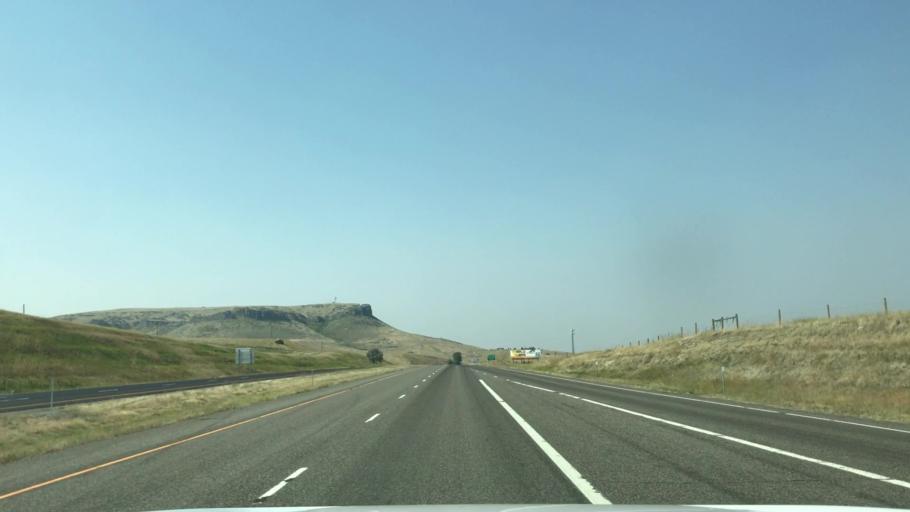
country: US
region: Montana
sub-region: Cascade County
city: Sun Prairie
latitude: 47.2637
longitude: -111.7079
